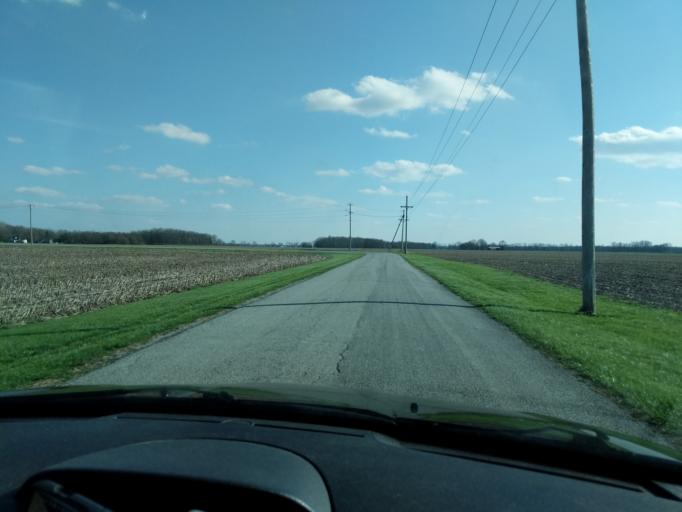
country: US
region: Ohio
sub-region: Champaign County
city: Urbana
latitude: 40.1388
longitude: -83.8158
